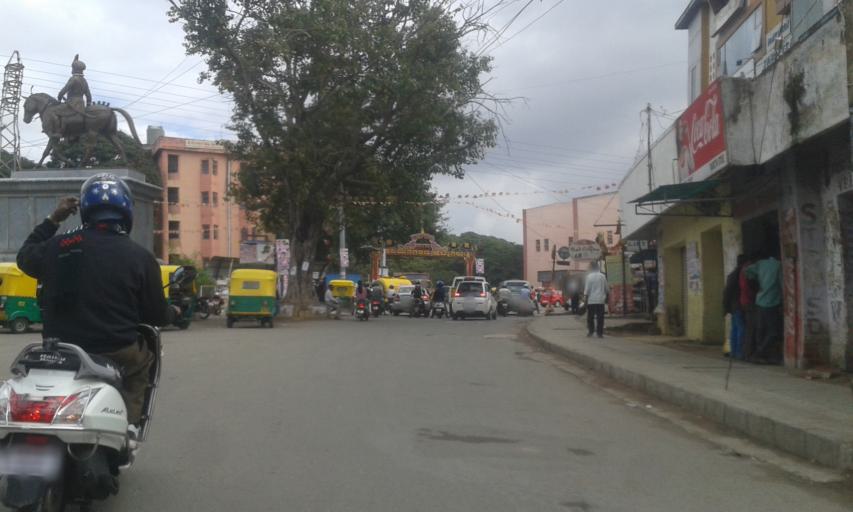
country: IN
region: Karnataka
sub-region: Bangalore Urban
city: Bangalore
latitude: 12.9715
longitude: 77.6581
